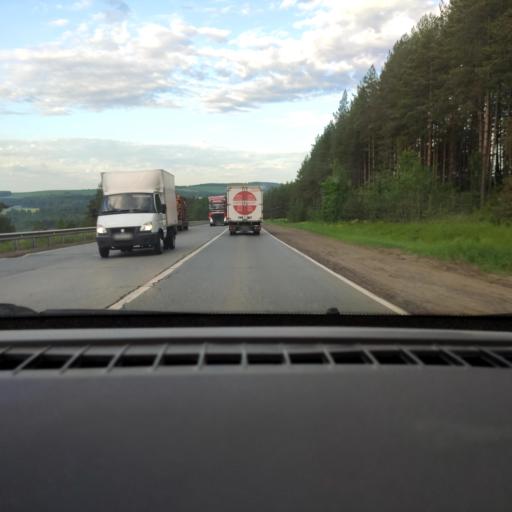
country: RU
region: Perm
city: Nytva
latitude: 57.9559
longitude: 55.1588
